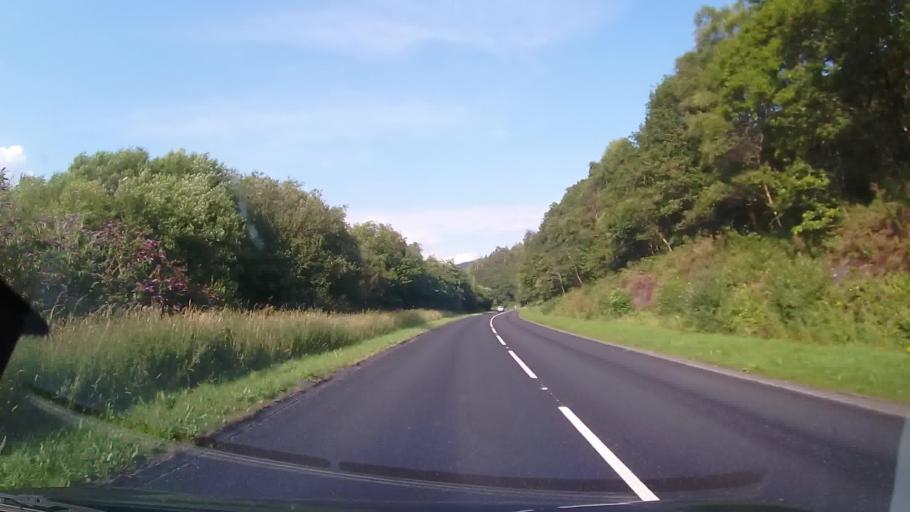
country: GB
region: Wales
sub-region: Gwynedd
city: Penrhyndeudraeth
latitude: 52.9358
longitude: -4.0568
